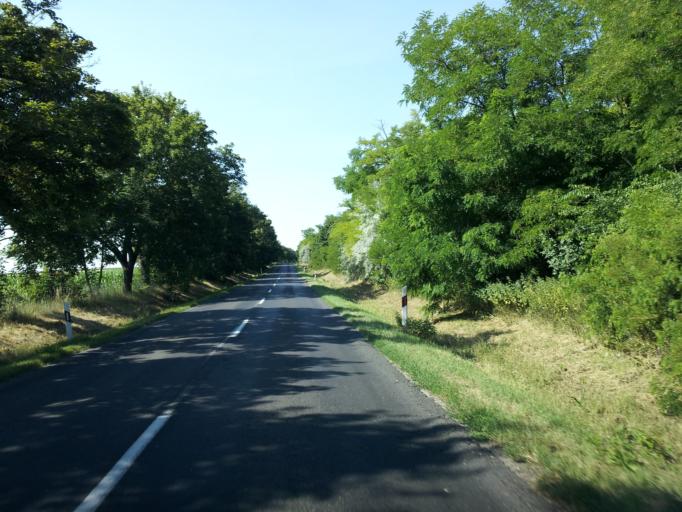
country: HU
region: Fejer
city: Lovasbereny
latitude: 47.3241
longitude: 18.5715
